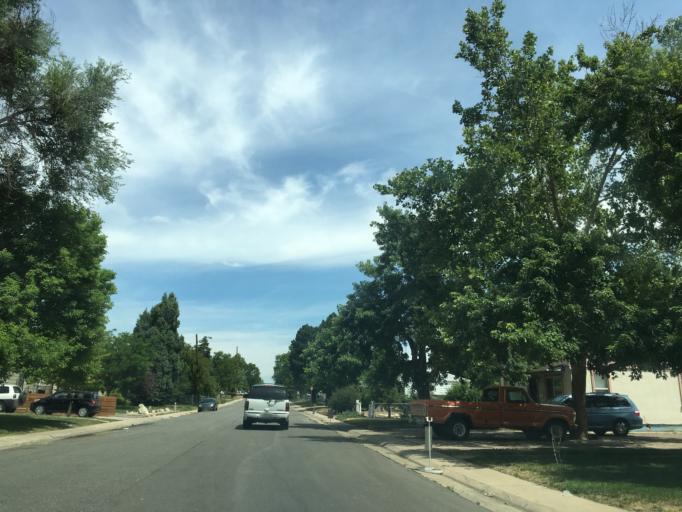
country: US
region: Colorado
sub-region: Jefferson County
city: Lakewood
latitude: 39.6933
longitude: -105.0414
